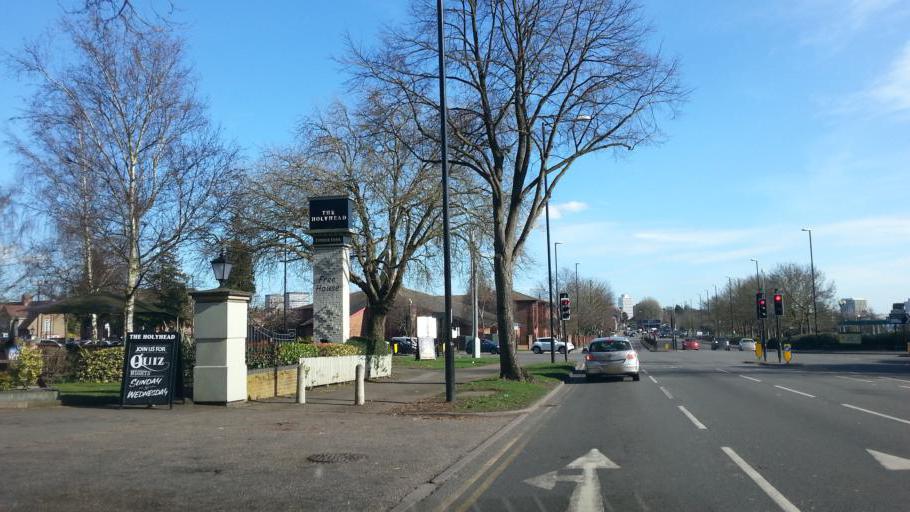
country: GB
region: England
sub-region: Coventry
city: Coventry
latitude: 52.4143
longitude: -1.5326
